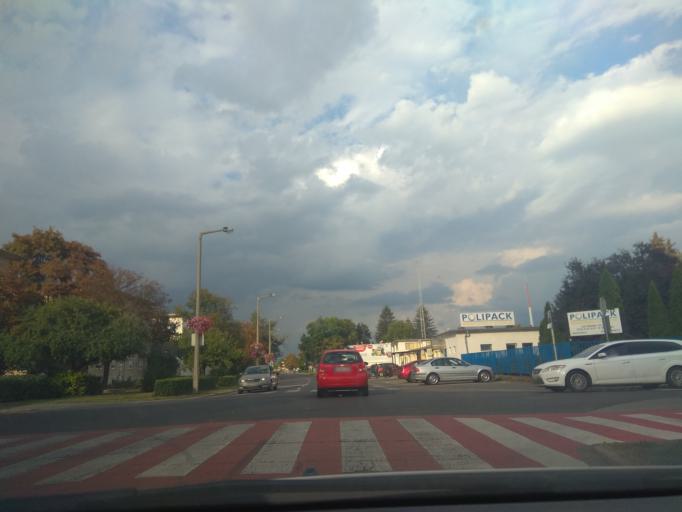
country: HU
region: Borsod-Abauj-Zemplen
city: Sajooeroes
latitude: 47.9285
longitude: 21.0441
